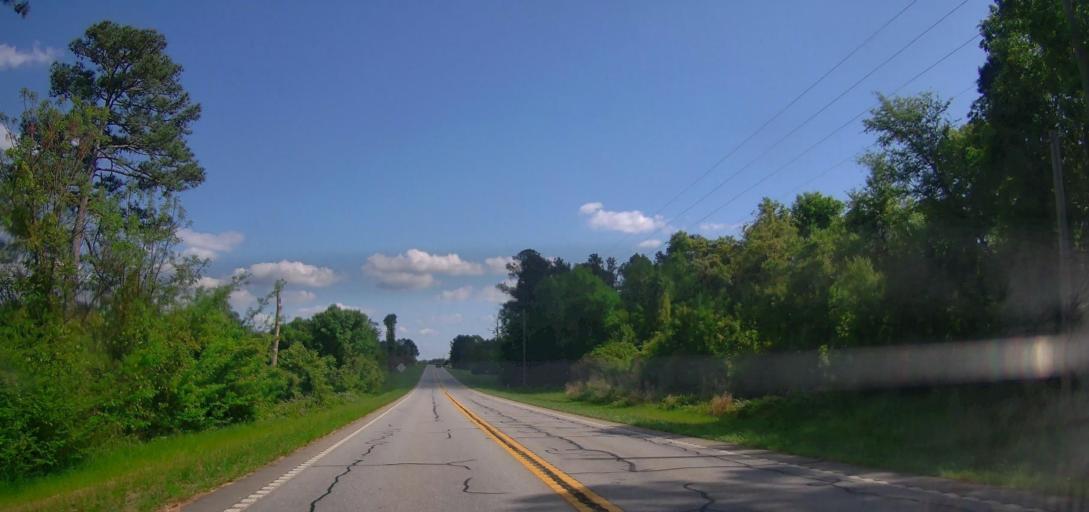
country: US
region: Georgia
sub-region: Greene County
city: Greensboro
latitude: 33.6048
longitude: -83.3085
